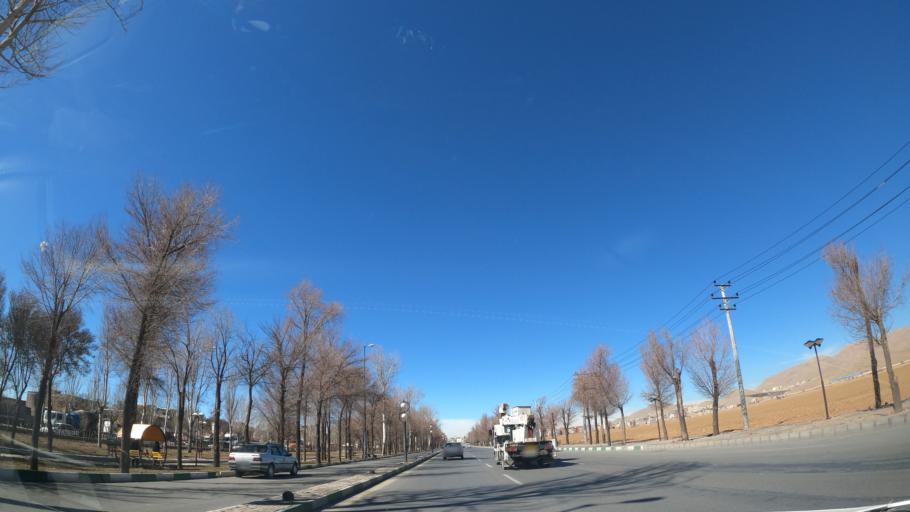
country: IR
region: Chahar Mahall va Bakhtiari
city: Shahrekord
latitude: 32.3084
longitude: 50.8988
